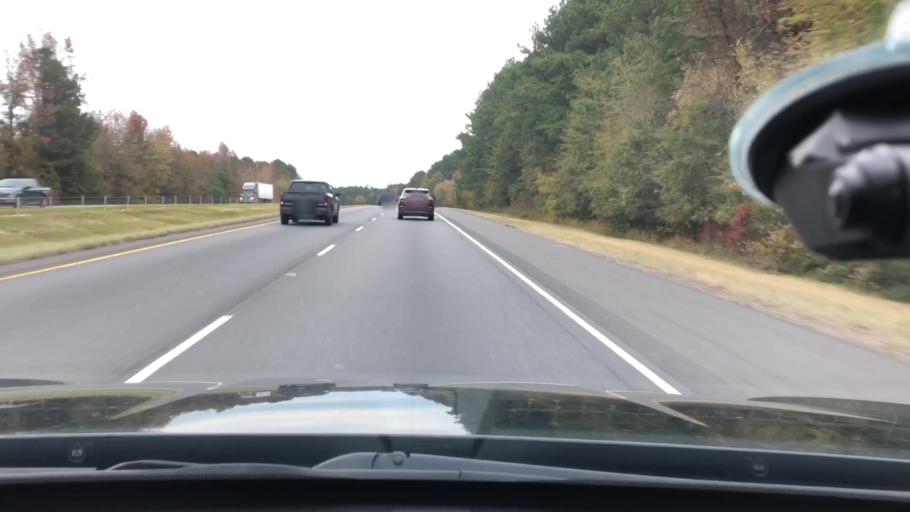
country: US
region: Arkansas
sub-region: Clark County
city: Gurdon
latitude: 34.0326
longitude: -93.1466
